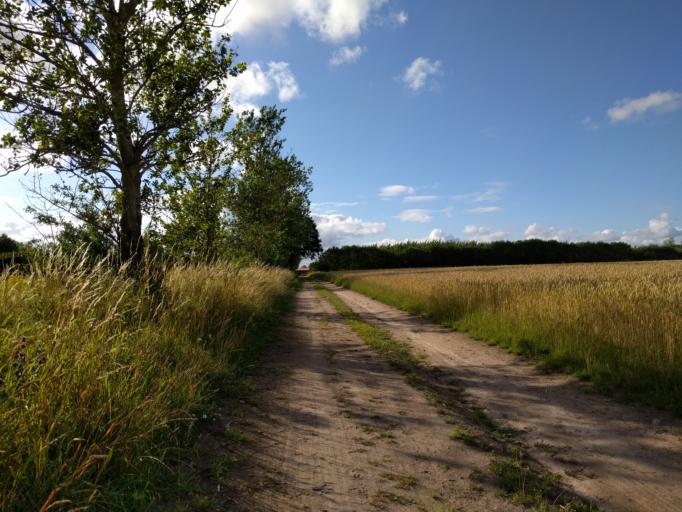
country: DK
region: South Denmark
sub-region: Kerteminde Kommune
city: Langeskov
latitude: 55.3890
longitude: 10.5498
